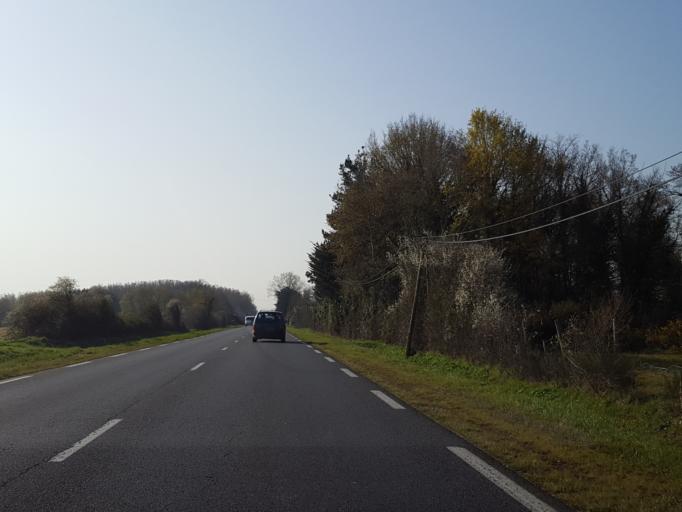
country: FR
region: Pays de la Loire
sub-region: Departement de la Loire-Atlantique
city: Geneston
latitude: 47.0765
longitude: -1.5229
